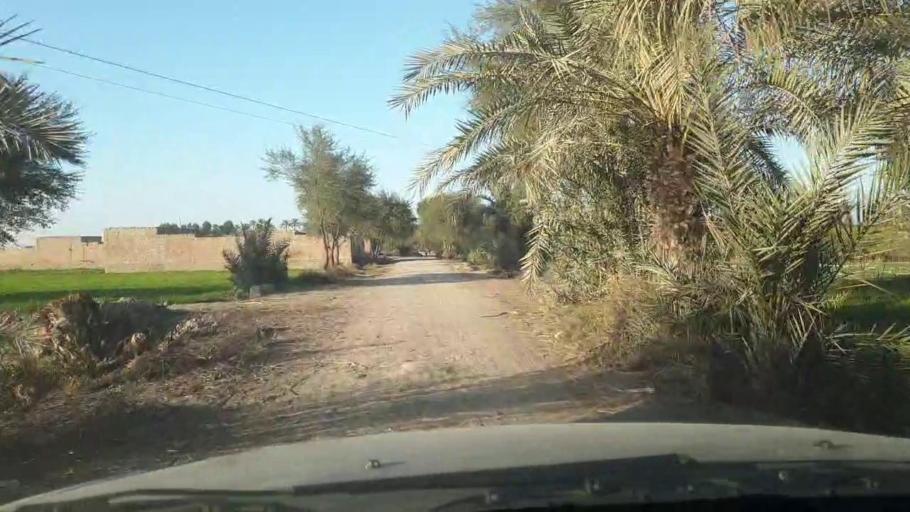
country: PK
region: Sindh
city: Ghotki
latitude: 28.0253
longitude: 69.3082
